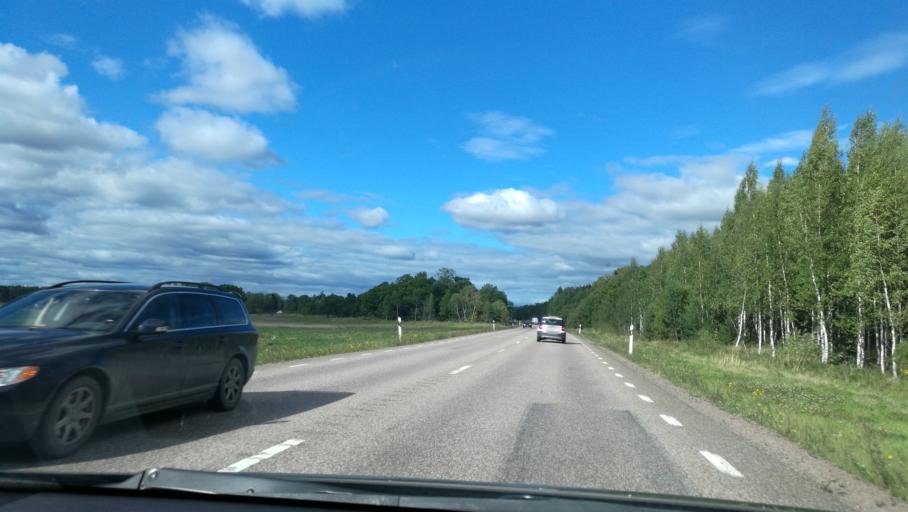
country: SE
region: Soedermanland
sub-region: Eskilstuna Kommun
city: Kvicksund
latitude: 59.4855
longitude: 16.3055
